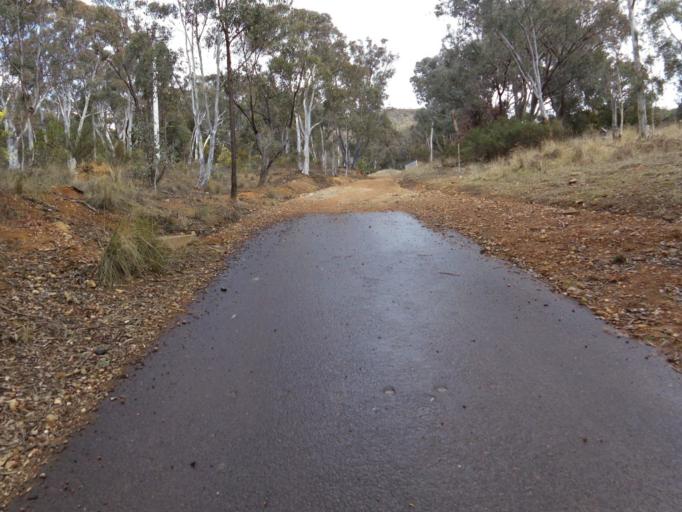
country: AU
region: Australian Capital Territory
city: Acton
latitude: -35.2709
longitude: 149.1074
